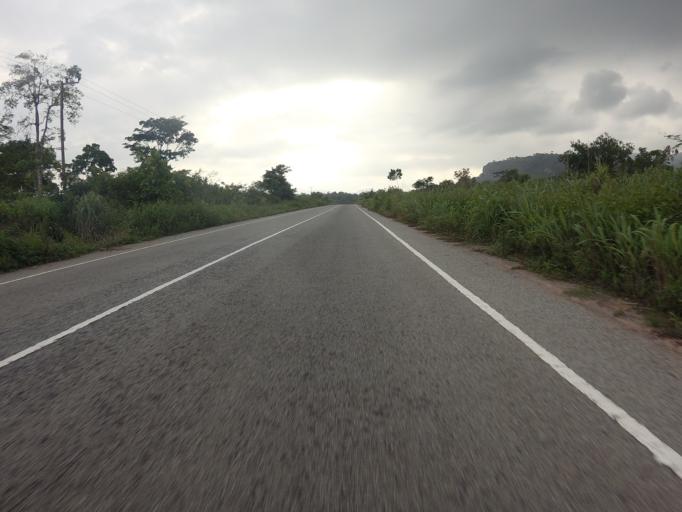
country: GH
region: Volta
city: Ho
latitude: 6.7843
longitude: 0.4576
